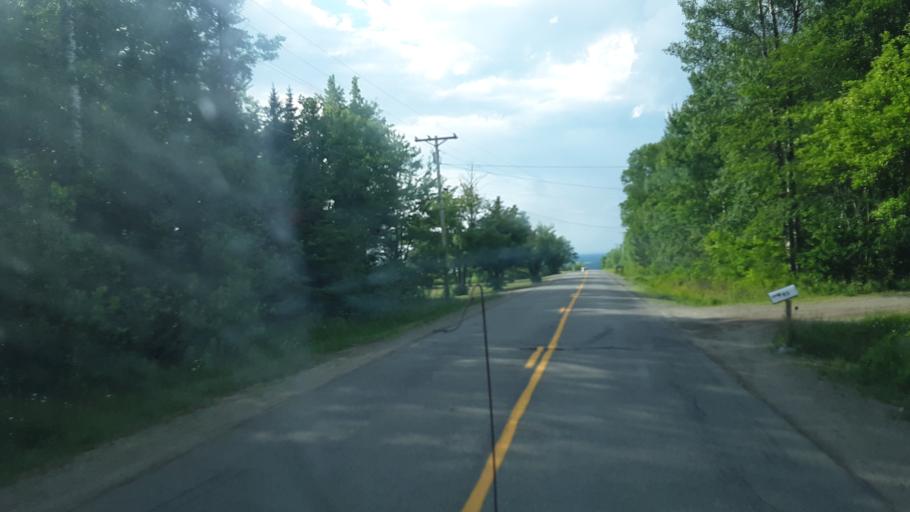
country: US
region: Maine
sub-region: Washington County
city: Calais
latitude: 45.0919
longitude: -67.5057
